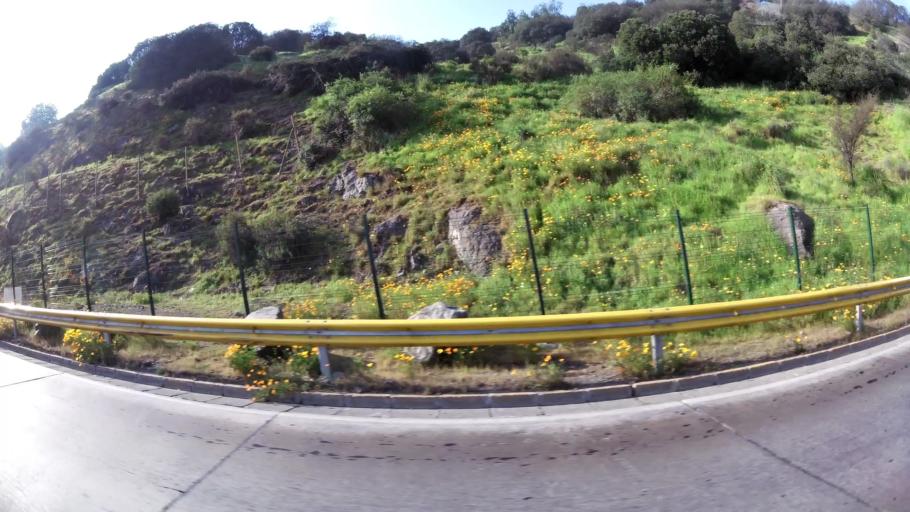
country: CL
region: Santiago Metropolitan
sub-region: Provincia de Santiago
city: Villa Presidente Frei, Nunoa, Santiago, Chile
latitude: -33.3755
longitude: -70.5395
